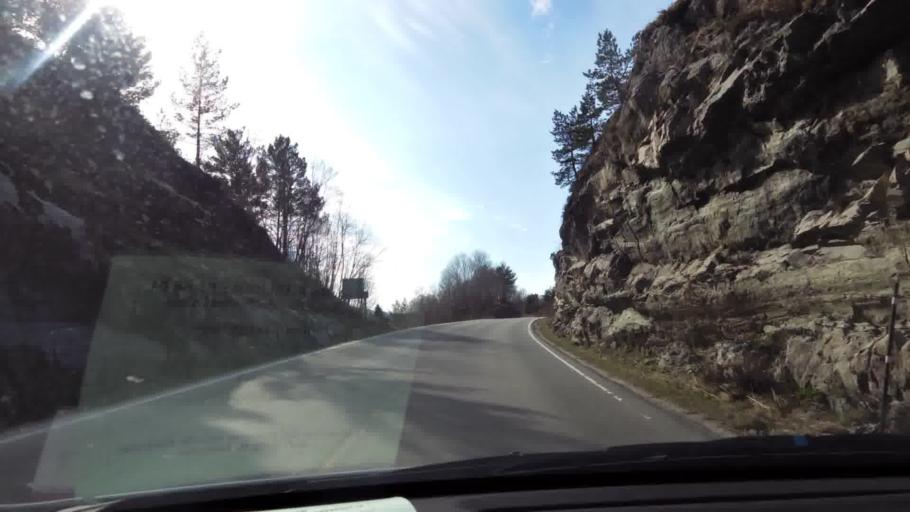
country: NO
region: More og Romsdal
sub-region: Kristiansund
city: Rensvik
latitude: 63.1106
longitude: 7.8630
